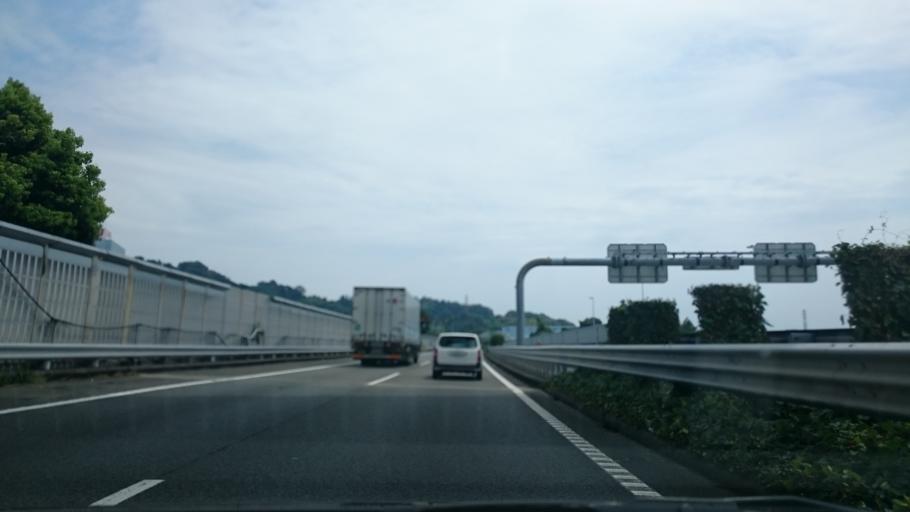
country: JP
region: Shizuoka
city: Shizuoka-shi
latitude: 35.0470
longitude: 138.4881
